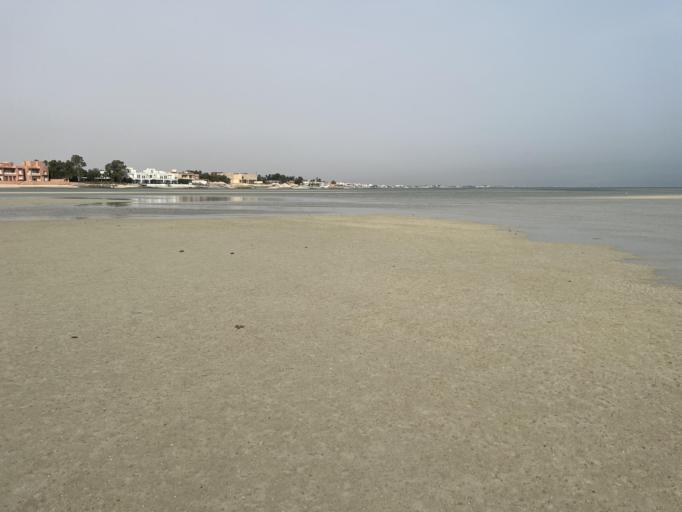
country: SA
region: Eastern Province
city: Al Khafji
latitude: 28.5502
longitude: 48.4221
